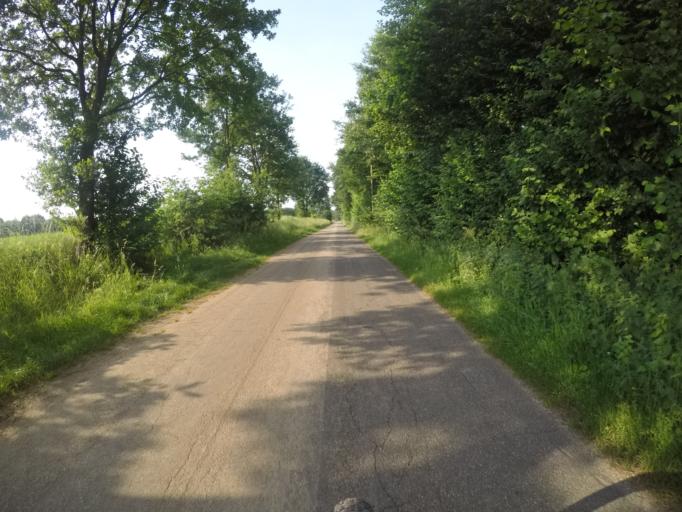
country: DE
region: North Rhine-Westphalia
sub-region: Regierungsbezirk Munster
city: Isselburg
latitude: 51.8294
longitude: 6.5083
